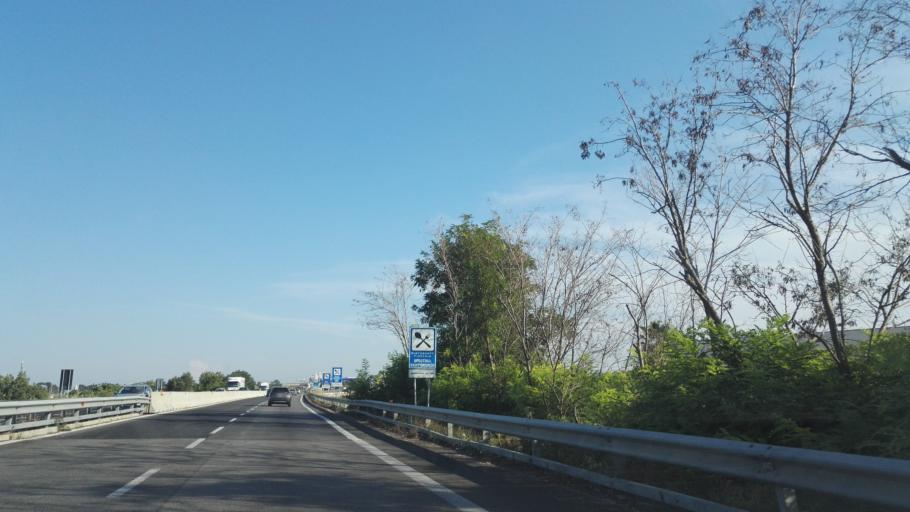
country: IT
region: Apulia
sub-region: Provincia di Bari
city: Polignano a Mare
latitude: 40.9972
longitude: 17.2027
